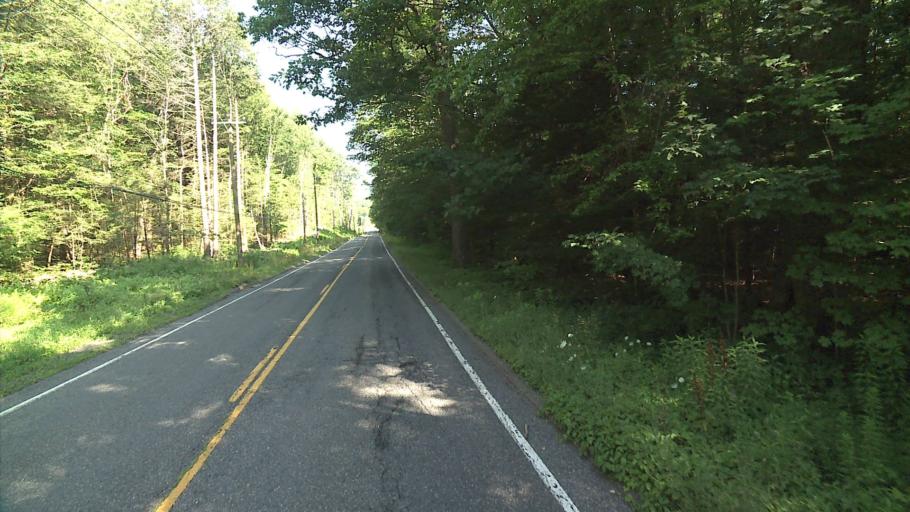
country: US
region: Connecticut
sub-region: Litchfield County
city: Winsted
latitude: 42.0111
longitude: -73.1103
